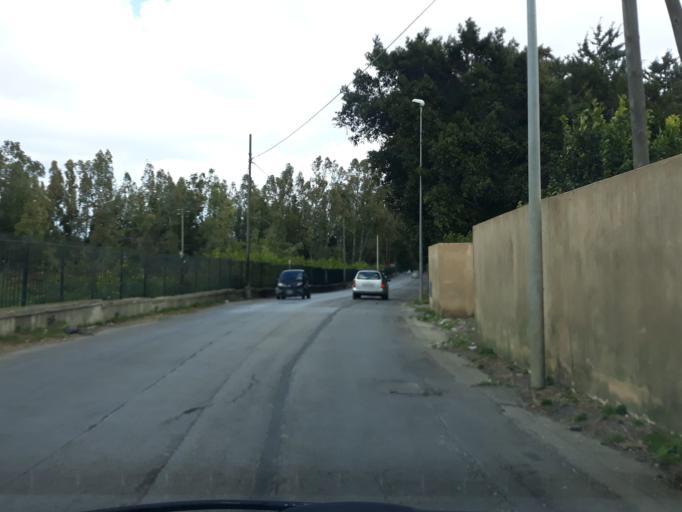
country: IT
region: Sicily
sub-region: Palermo
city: Palermo
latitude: 38.1185
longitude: 13.3046
